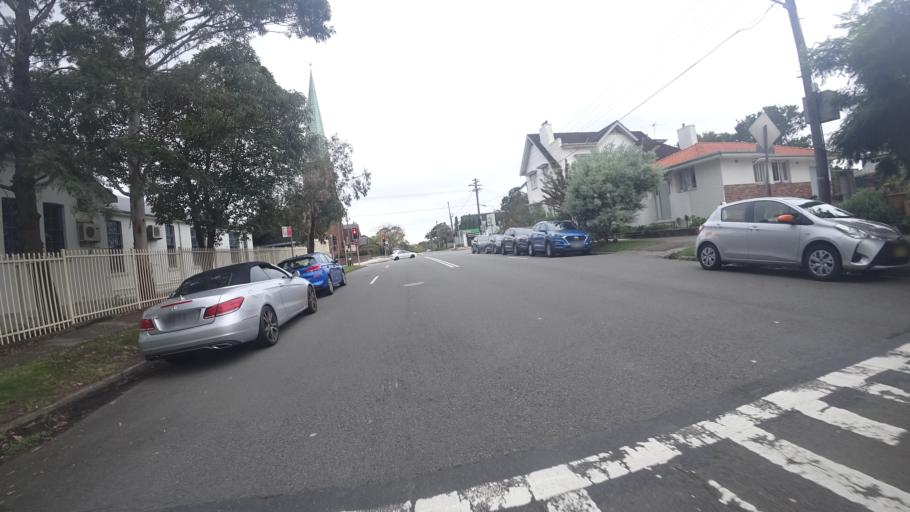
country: AU
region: New South Wales
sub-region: North Sydney
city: St Leonards
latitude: -33.8196
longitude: 151.2003
